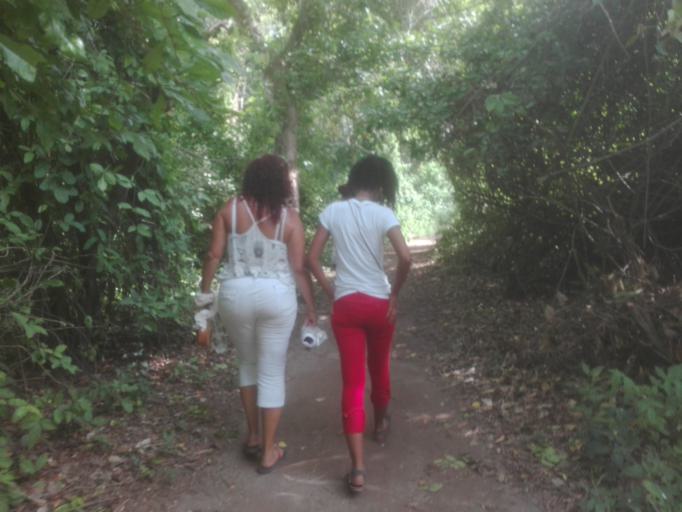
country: CO
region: Bolivar
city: Turbana
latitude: 10.1789
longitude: -75.7398
